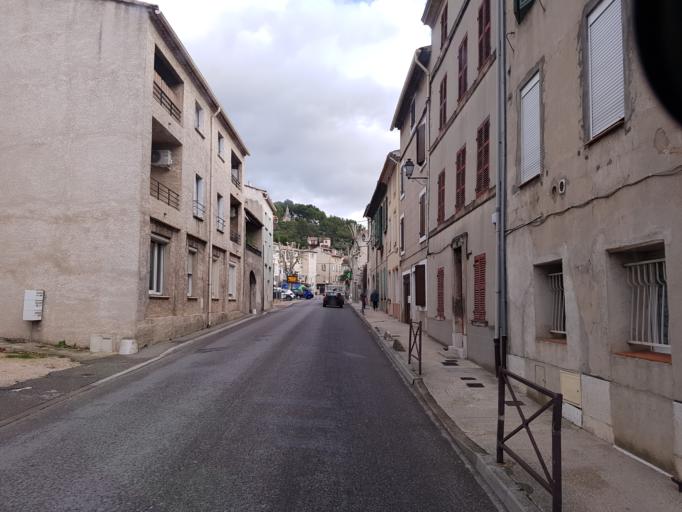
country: FR
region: Provence-Alpes-Cote d'Azur
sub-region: Departement des Bouches-du-Rhone
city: Cuges-les-Pins
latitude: 43.2757
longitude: 5.6989
